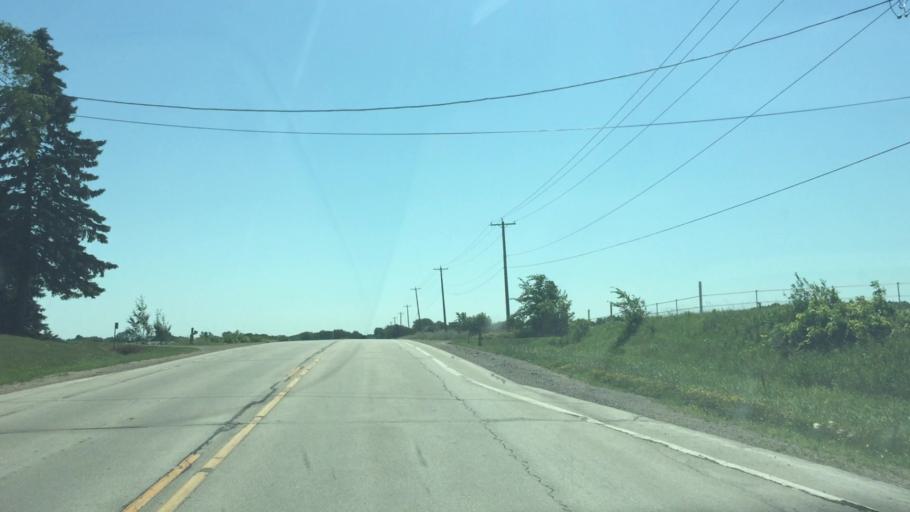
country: US
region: Wisconsin
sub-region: Calumet County
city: Hilbert
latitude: 44.1402
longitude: -88.1841
